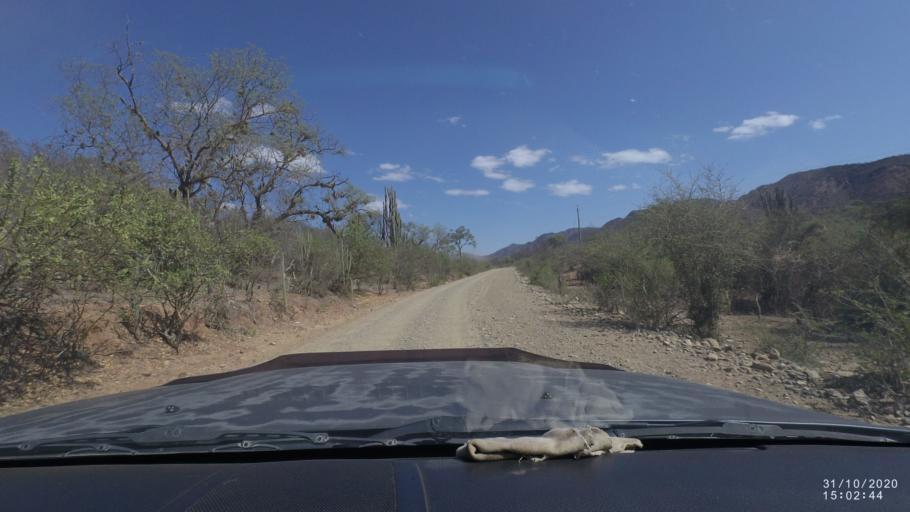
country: BO
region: Cochabamba
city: Aiquile
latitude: -18.2708
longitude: -64.8106
